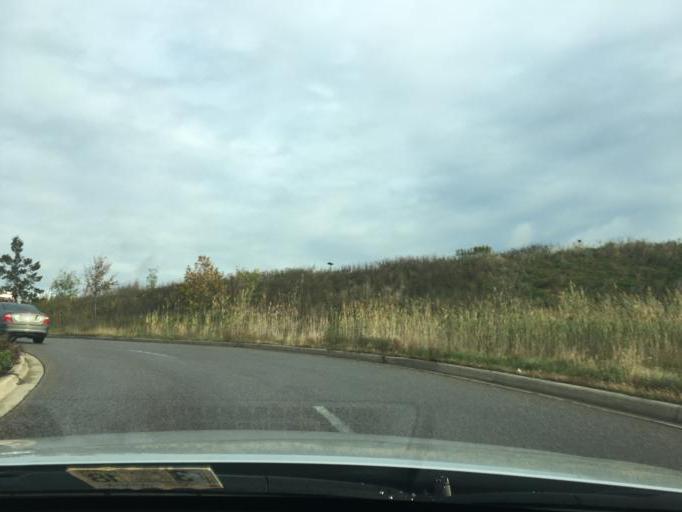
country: US
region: Michigan
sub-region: Wayne County
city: Allen Park
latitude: 42.2778
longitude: -83.2075
